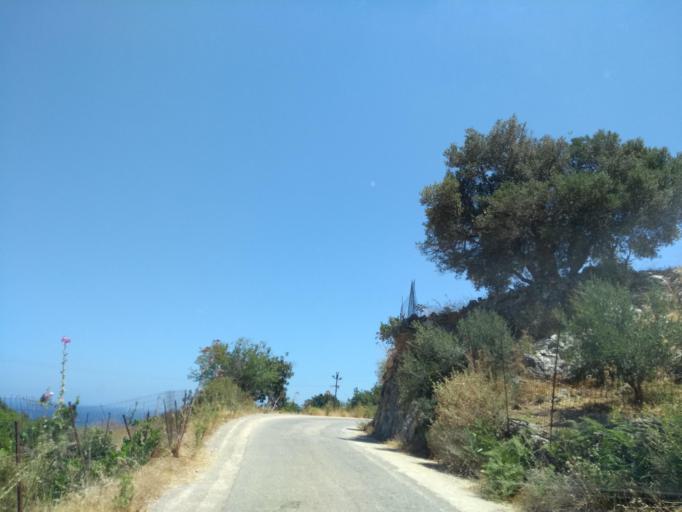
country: GR
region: Crete
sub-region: Nomos Chanias
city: Georgioupolis
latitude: 35.3180
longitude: 24.2893
